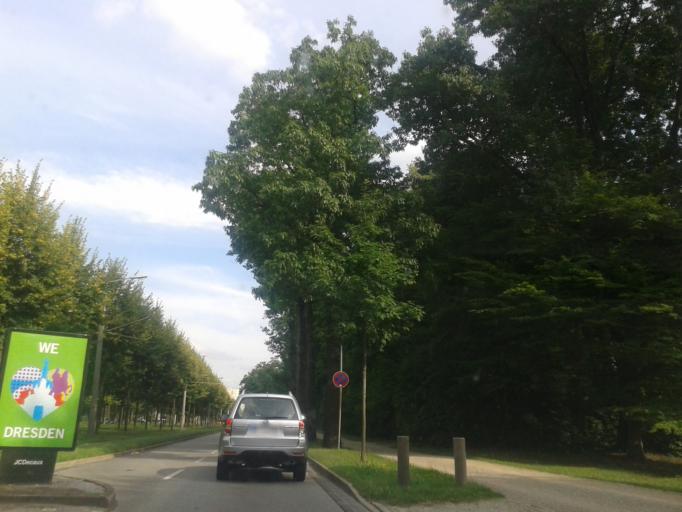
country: DE
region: Saxony
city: Dresden
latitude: 51.0394
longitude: 13.7717
